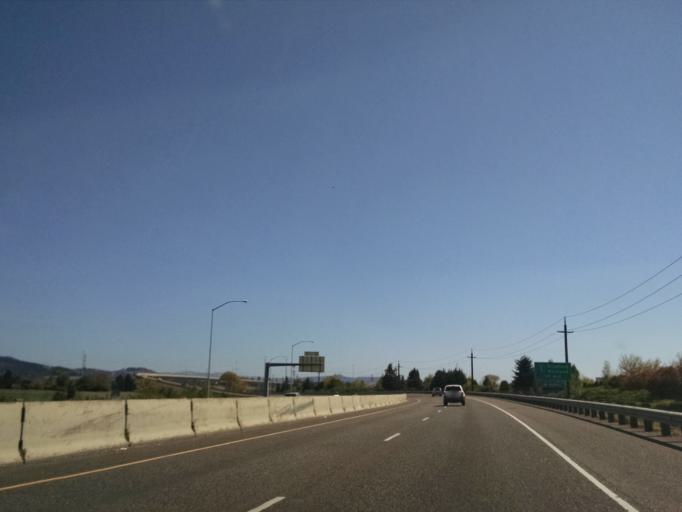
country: US
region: Oregon
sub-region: Lane County
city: Eugene
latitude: 44.0851
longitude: -123.0584
